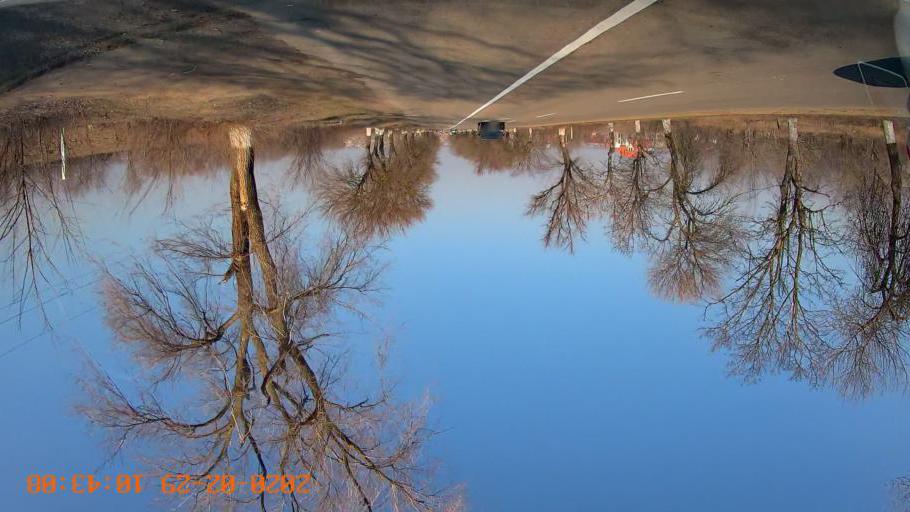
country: MD
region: Telenesti
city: Grigoriopol
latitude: 47.0580
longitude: 29.4049
